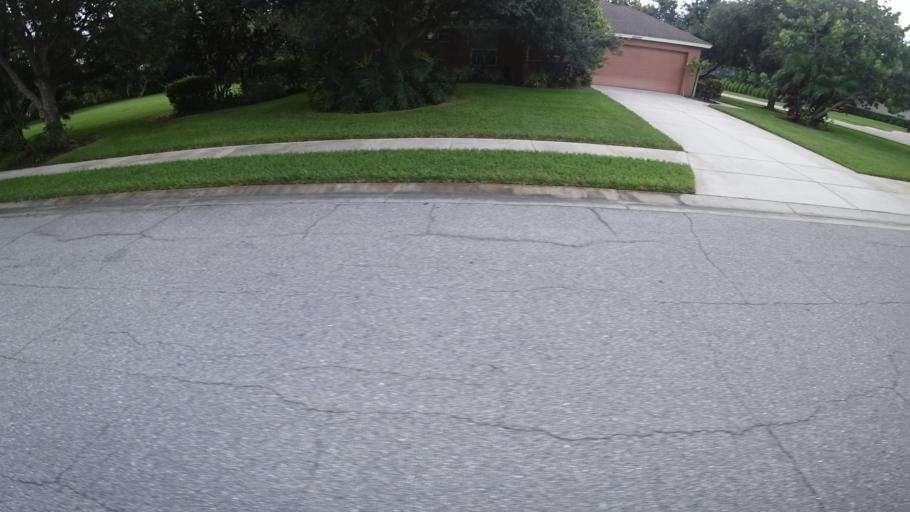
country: US
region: Florida
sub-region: Sarasota County
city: The Meadows
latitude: 27.4099
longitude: -82.4348
